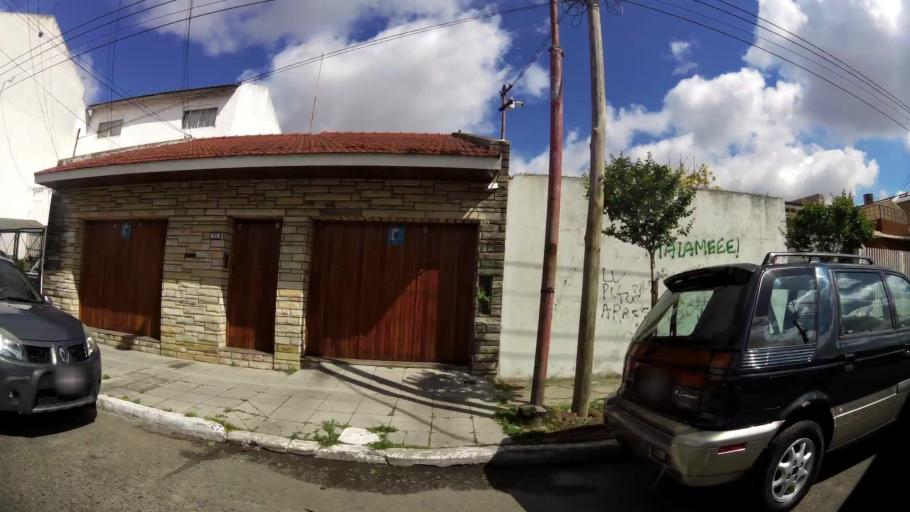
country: AR
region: Buenos Aires
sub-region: Partido de Lanus
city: Lanus
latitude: -34.6943
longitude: -58.4092
